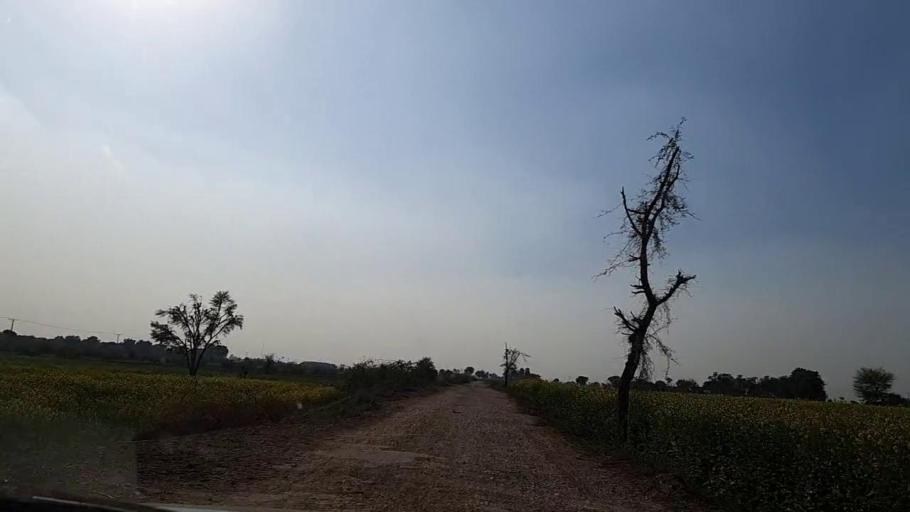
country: PK
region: Sindh
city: Sakrand
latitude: 26.1278
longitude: 68.2611
